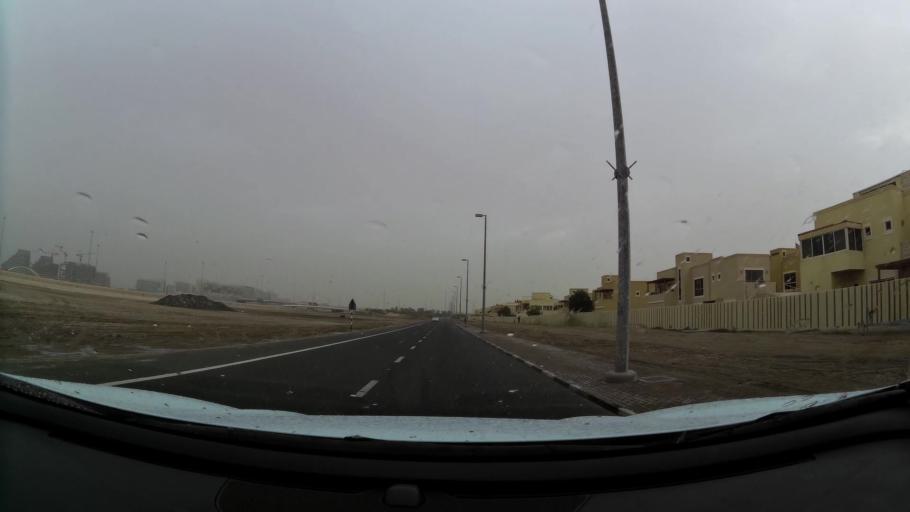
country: AE
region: Abu Dhabi
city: Abu Dhabi
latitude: 24.4419
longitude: 54.5962
